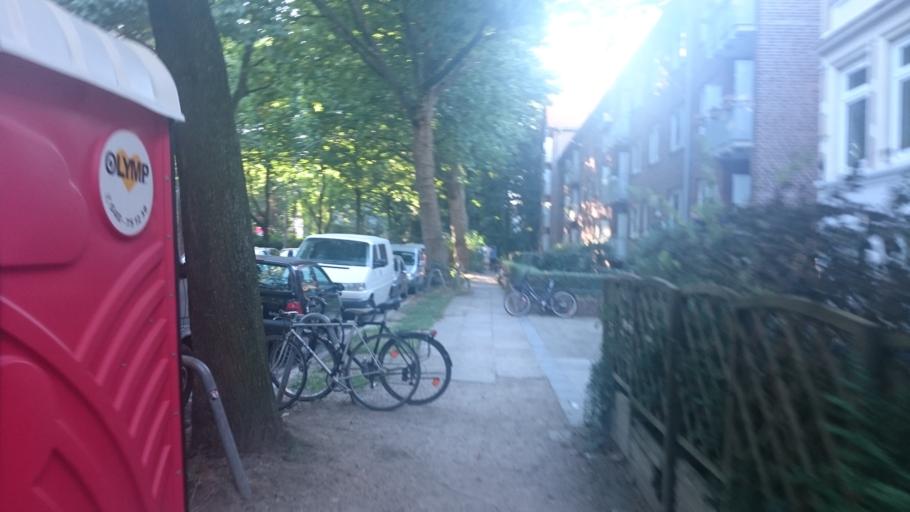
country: DE
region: Hamburg
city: Eimsbuettel
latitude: 53.5770
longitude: 9.9669
